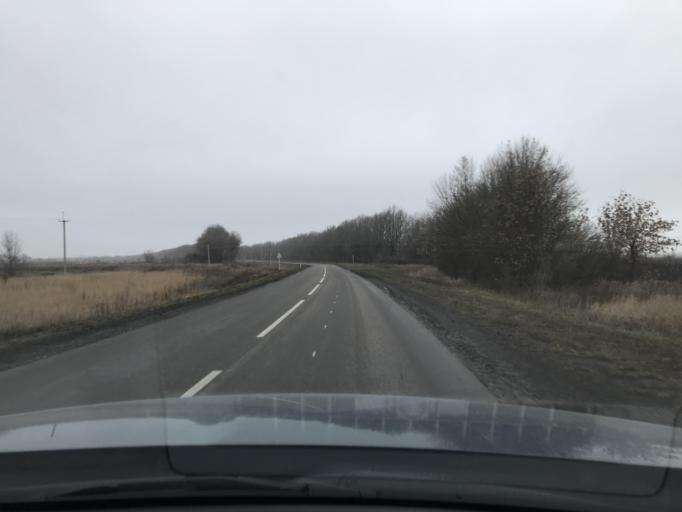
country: RU
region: Penza
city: Zemetchino
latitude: 53.5424
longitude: 42.6690
